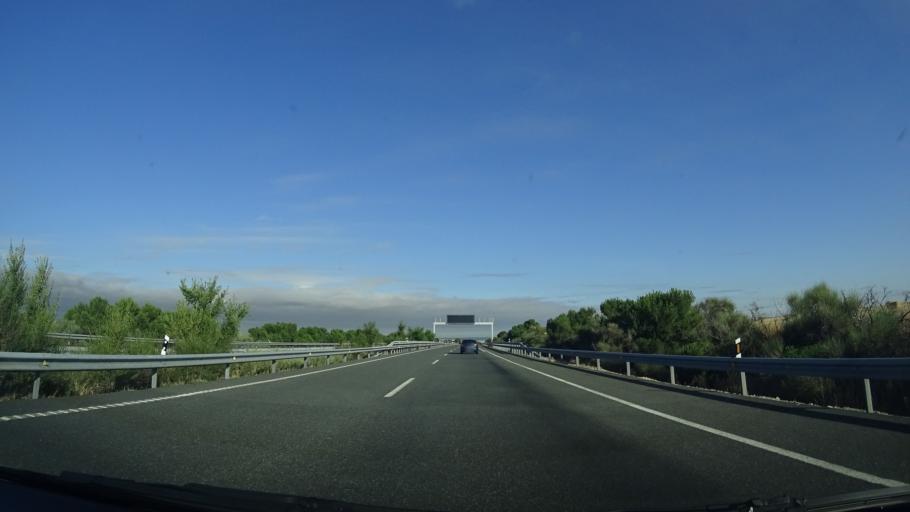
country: ES
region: Castille and Leon
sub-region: Provincia de Avila
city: Maello
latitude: 40.8239
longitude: -4.5134
